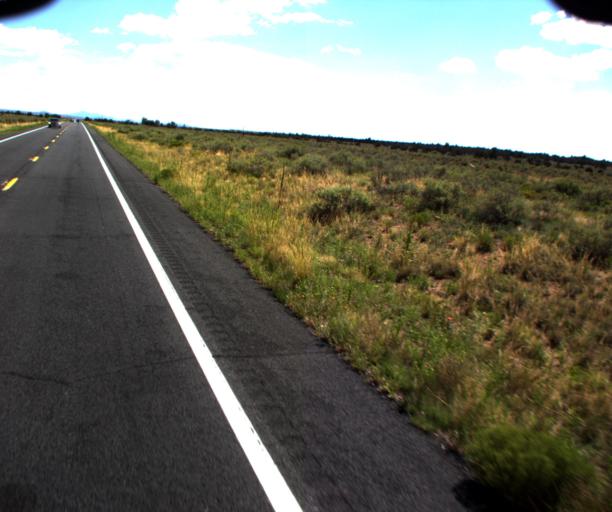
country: US
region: Arizona
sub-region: Coconino County
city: Grand Canyon Village
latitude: 35.6824
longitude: -112.1354
